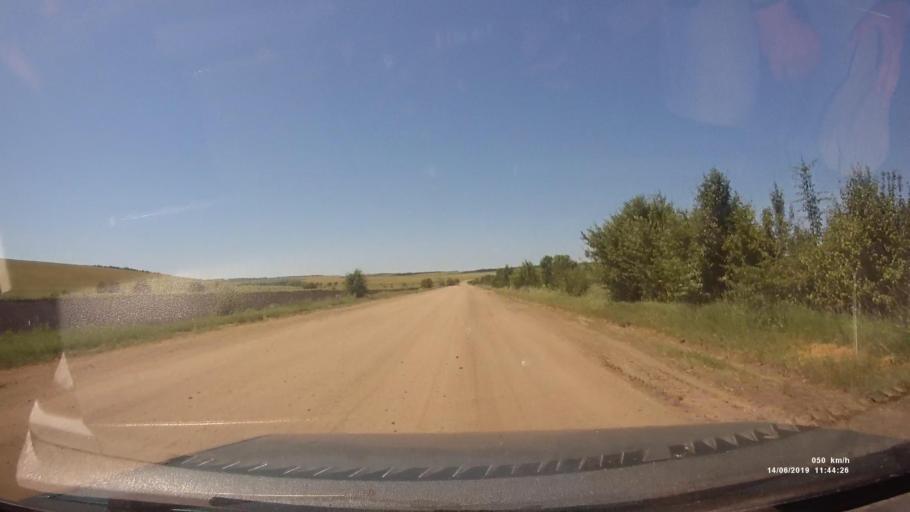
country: RU
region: Rostov
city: Kazanskaya
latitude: 49.8545
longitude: 41.3240
